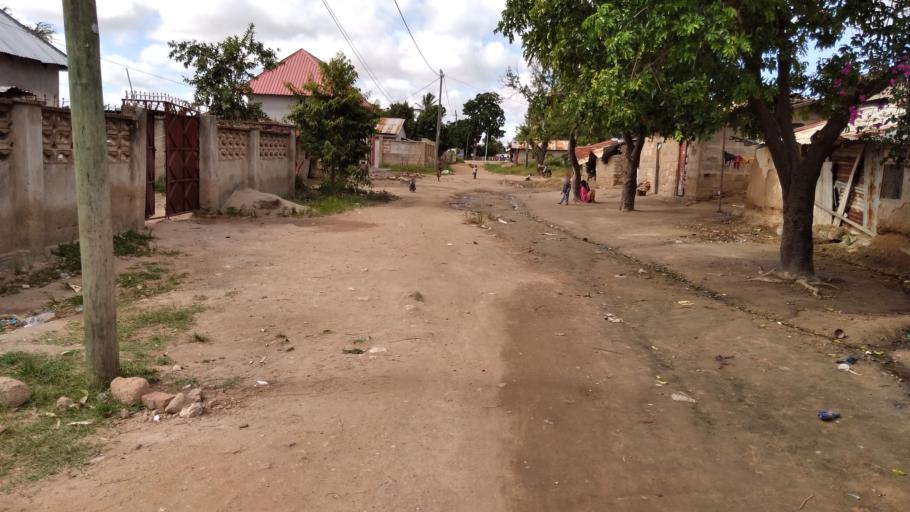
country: TZ
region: Dodoma
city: Dodoma
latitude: -6.1587
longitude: 35.7398
